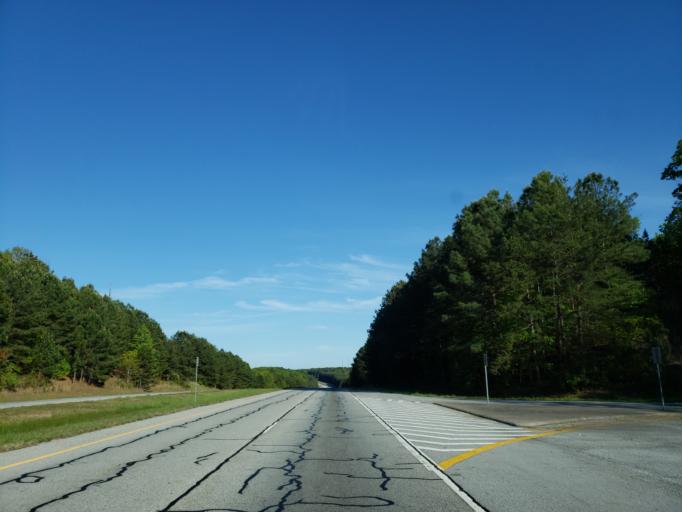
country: US
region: Georgia
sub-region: Polk County
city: Rockmart
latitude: 33.9356
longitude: -84.9690
